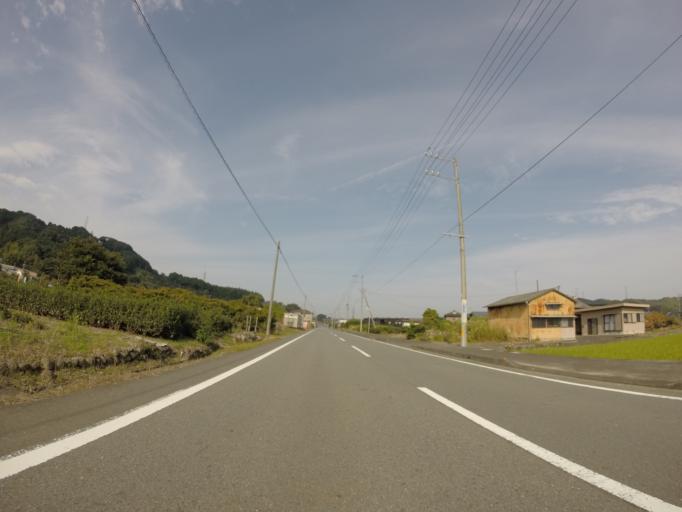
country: JP
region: Shizuoka
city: Shimada
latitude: 34.7664
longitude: 138.1844
